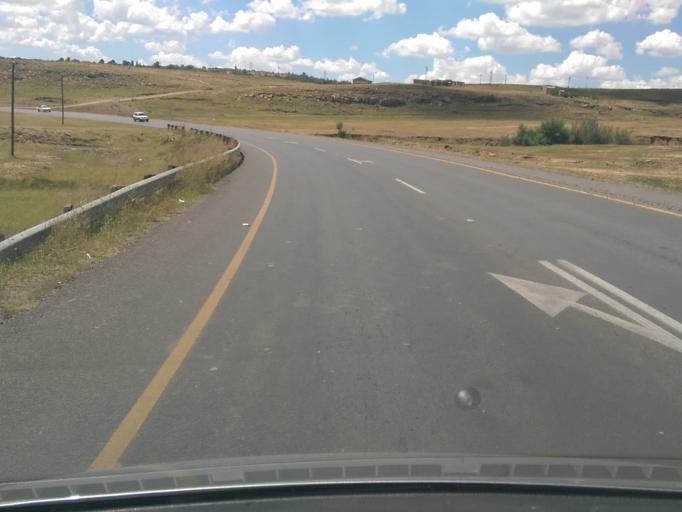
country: LS
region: Maseru
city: Maseru
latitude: -29.3890
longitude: 27.5048
